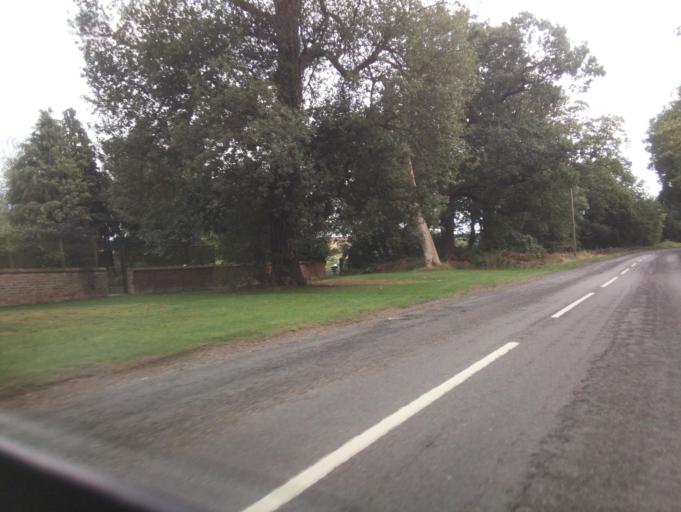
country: GB
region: England
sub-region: Nottinghamshire
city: East Leake
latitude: 52.8040
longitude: -1.1893
